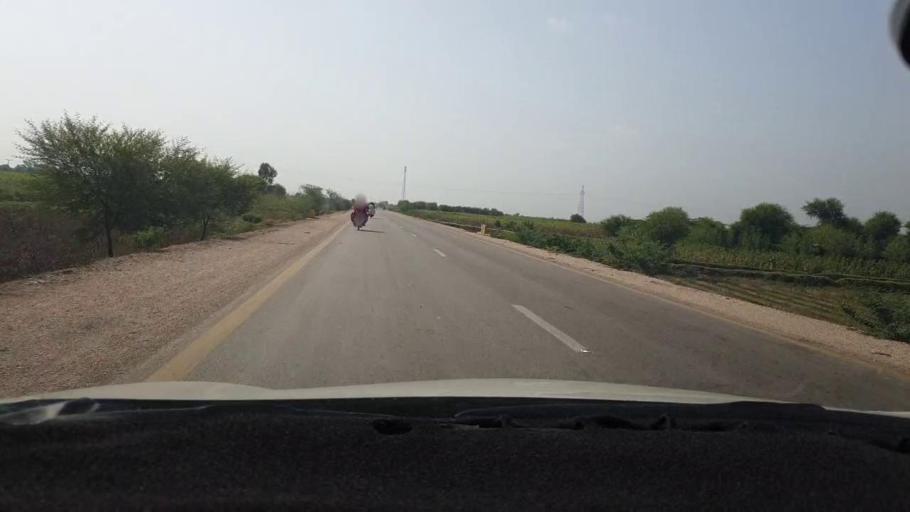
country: PK
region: Sindh
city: Tando Mittha Khan
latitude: 25.8343
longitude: 69.0632
